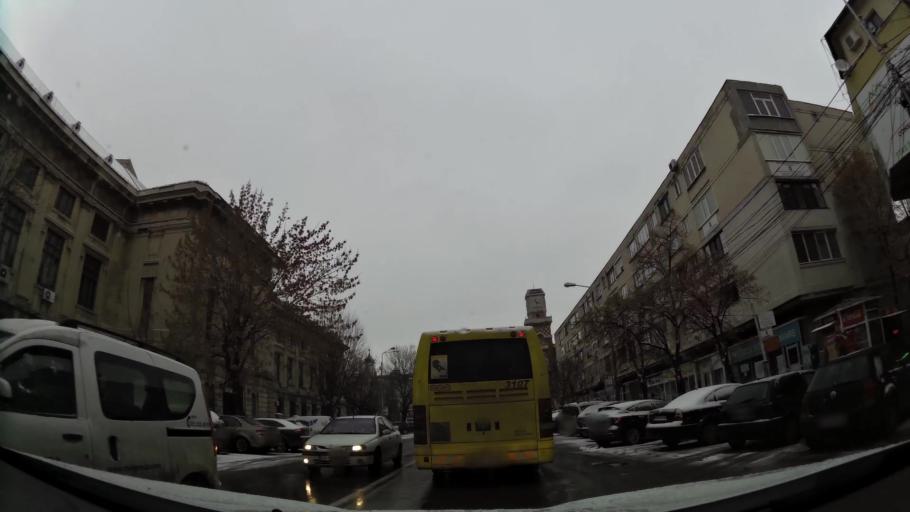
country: RO
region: Prahova
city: Ploiesti
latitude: 44.9424
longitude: 26.0225
